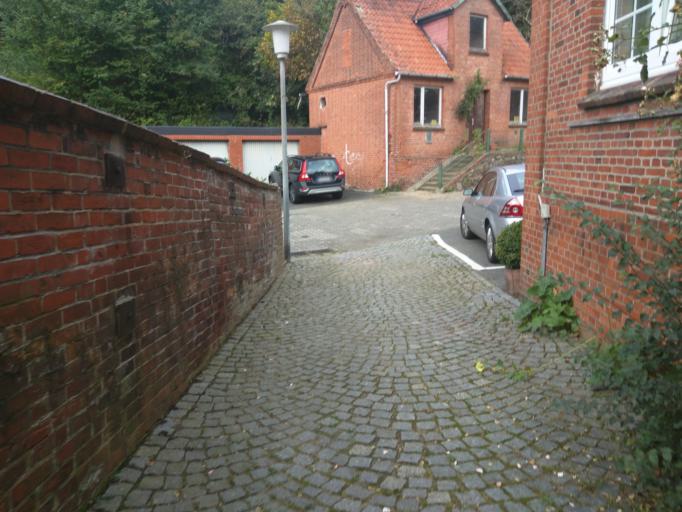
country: DE
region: Schleswig-Holstein
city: Lauenburg
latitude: 53.3723
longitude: 10.5536
